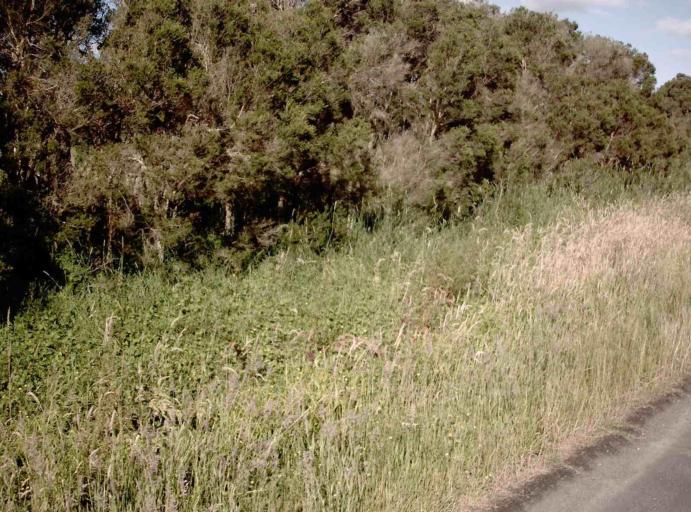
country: AU
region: Victoria
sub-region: Bass Coast
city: North Wonthaggi
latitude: -38.6272
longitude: 145.7154
